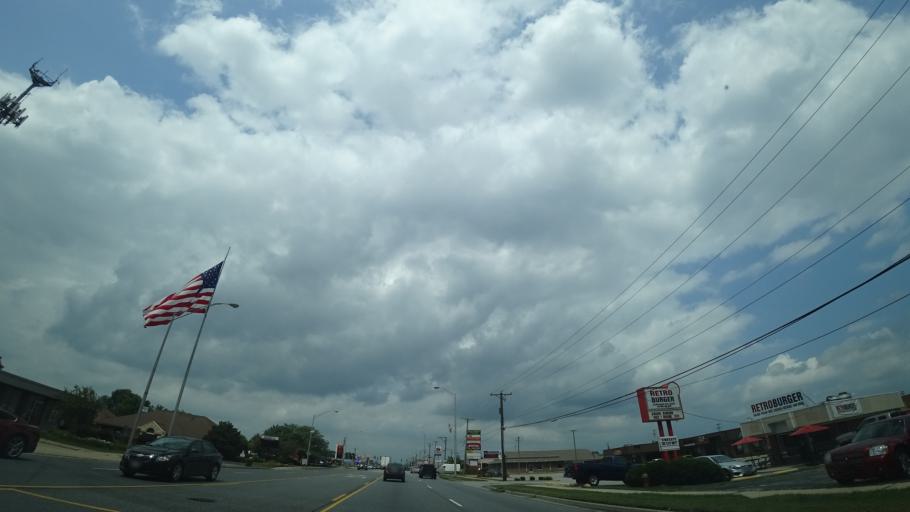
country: US
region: Illinois
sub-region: Cook County
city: Crestwood
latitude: 41.6411
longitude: -87.7378
